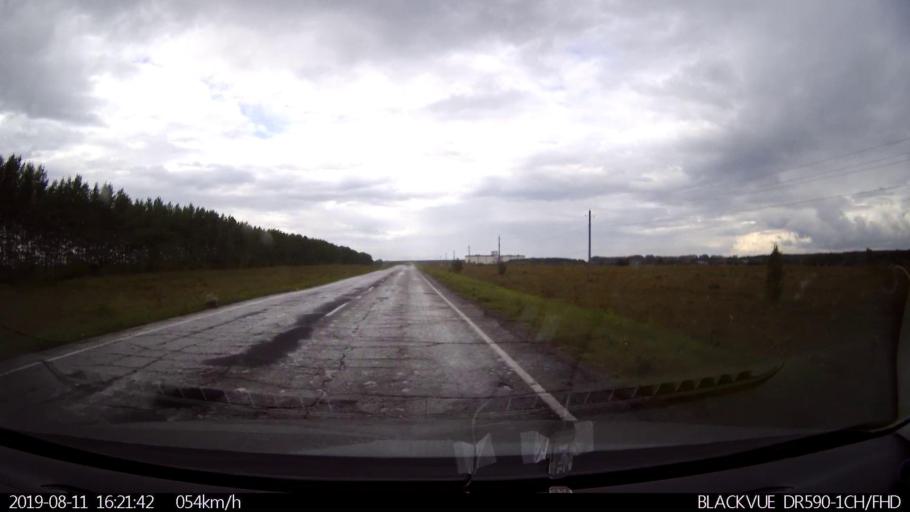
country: RU
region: Ulyanovsk
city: Mayna
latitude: 54.0819
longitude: 47.5967
